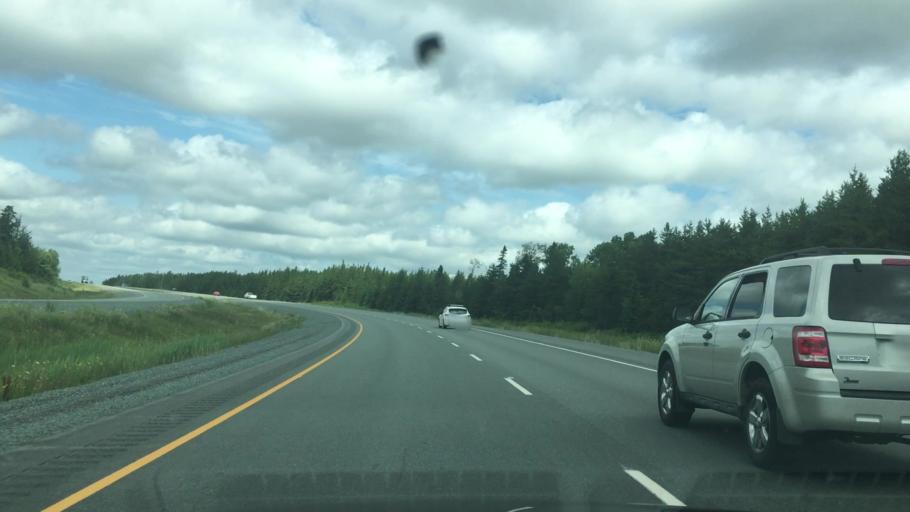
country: CA
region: Nova Scotia
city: Oxford
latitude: 45.6626
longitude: -63.7438
